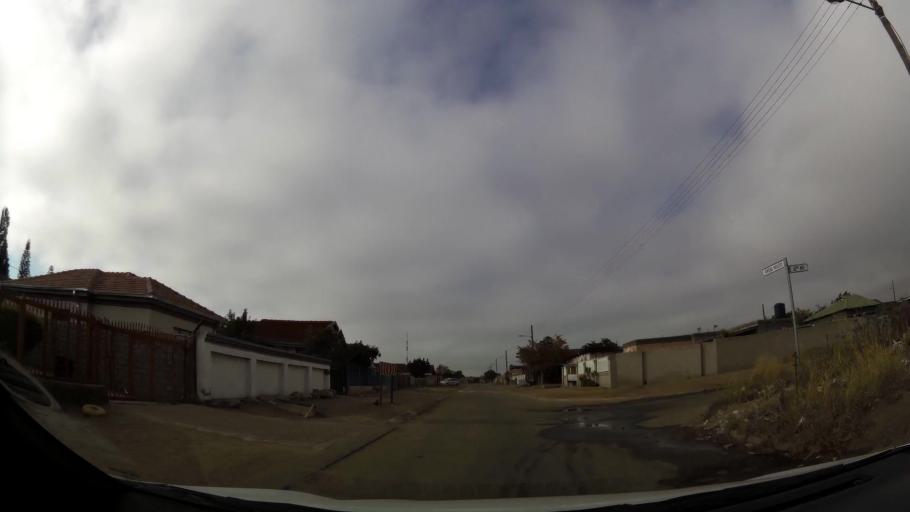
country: ZA
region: Limpopo
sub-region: Capricorn District Municipality
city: Polokwane
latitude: -23.8431
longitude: 29.3866
